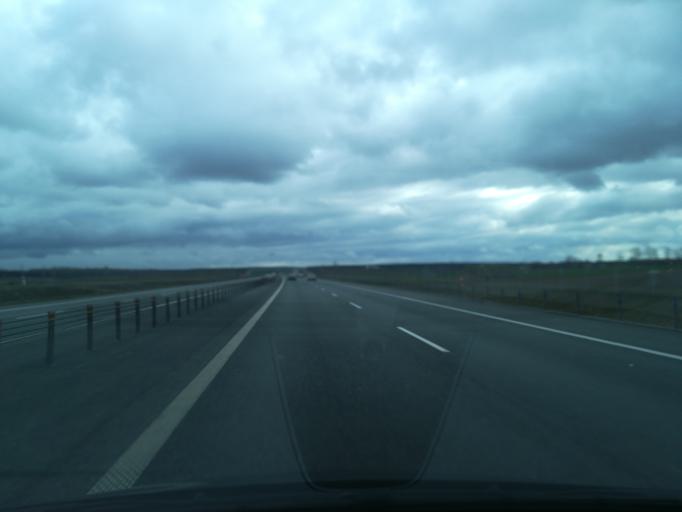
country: PL
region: Kujawsko-Pomorskie
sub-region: Powiat wabrzeski
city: Pluznica
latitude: 53.1759
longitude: 18.7386
